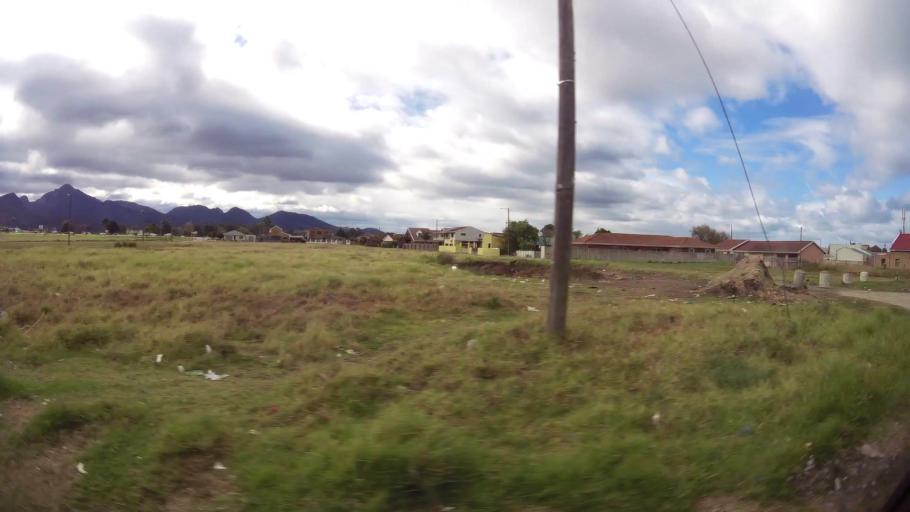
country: ZA
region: Western Cape
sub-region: Eden District Municipality
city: George
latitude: -33.9759
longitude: 22.4897
